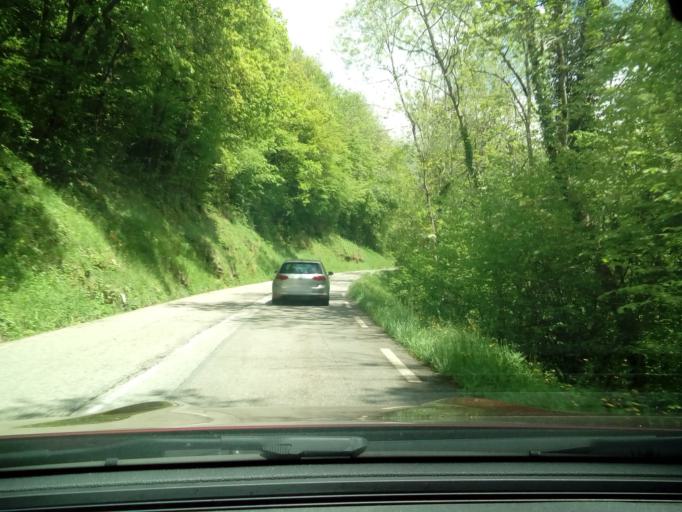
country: FR
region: Rhone-Alpes
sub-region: Departement de la Savoie
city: Barby
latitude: 45.5956
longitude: 6.0149
